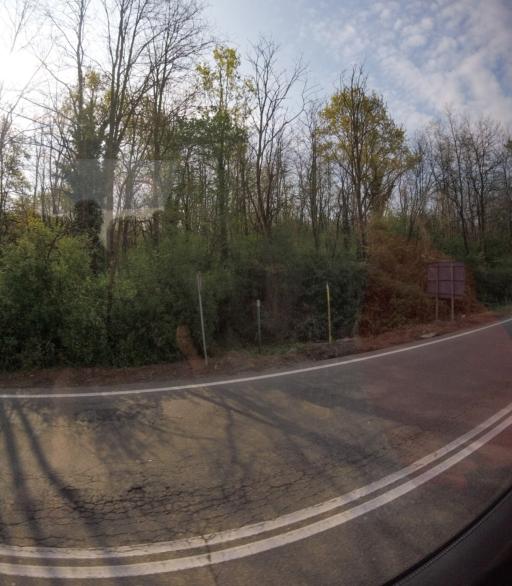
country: IT
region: Piedmont
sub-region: Provincia di Novara
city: Paruzzaro
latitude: 45.7333
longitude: 8.5023
